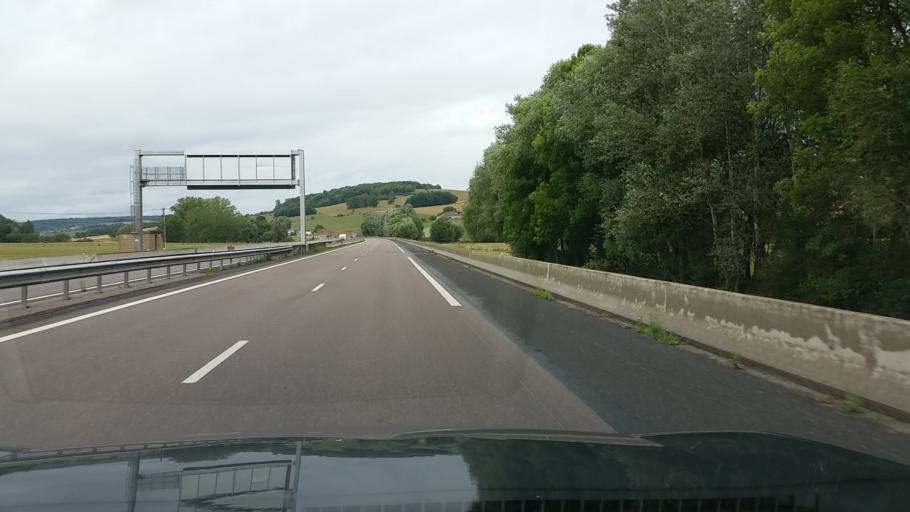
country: FR
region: Lorraine
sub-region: Departement des Vosges
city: Chatenois
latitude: 48.3226
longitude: 5.8558
